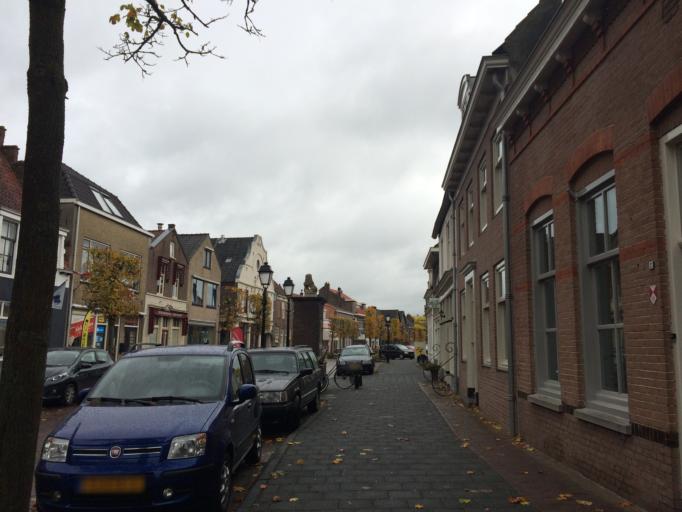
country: NL
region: Gelderland
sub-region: Gemeente Culemborg
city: Culemborg
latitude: 51.9548
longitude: 5.2272
